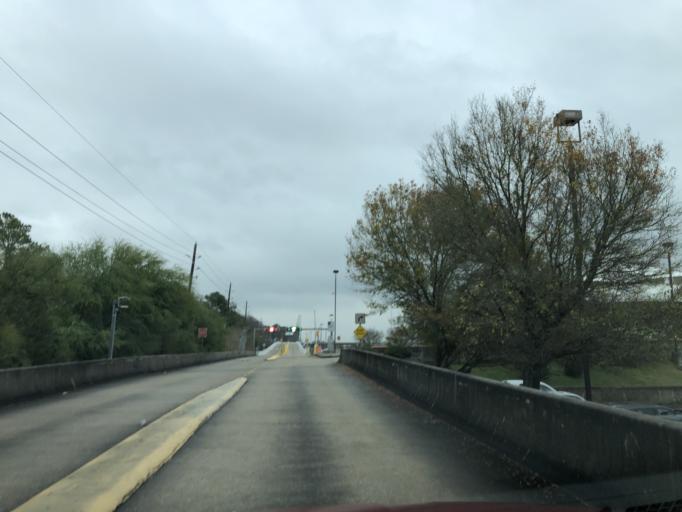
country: US
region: Texas
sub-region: Harris County
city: Aldine
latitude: 29.9740
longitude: -95.4263
